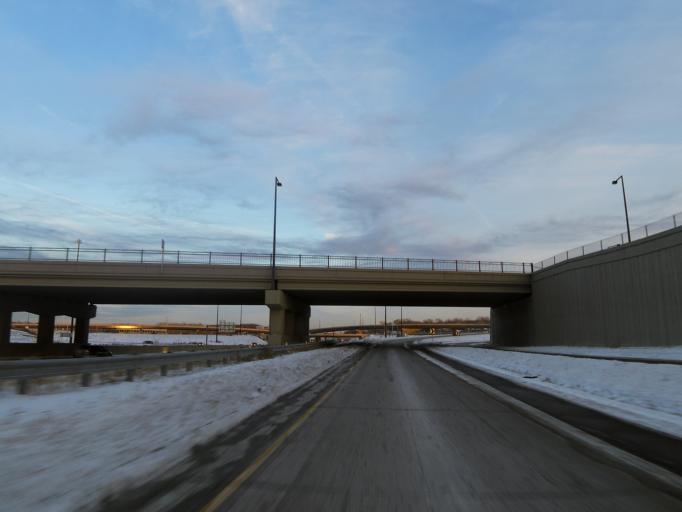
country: US
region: Minnesota
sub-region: Hennepin County
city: Edina
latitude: 44.8591
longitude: -93.3995
